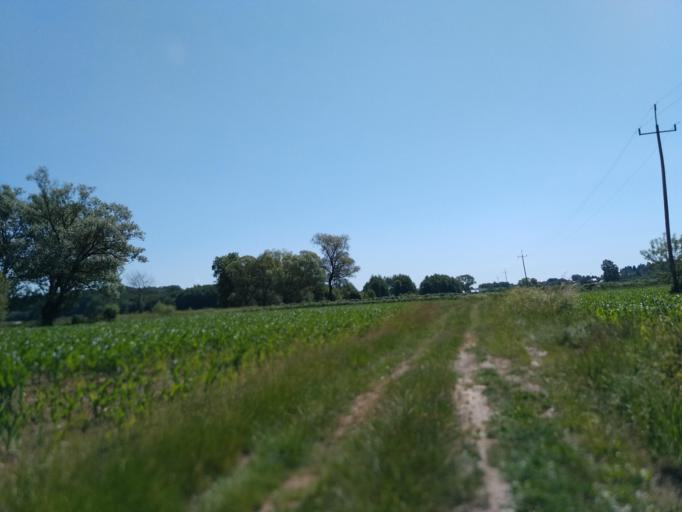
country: PL
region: Subcarpathian Voivodeship
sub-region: Krosno
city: Krosno
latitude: 49.7182
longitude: 21.7733
